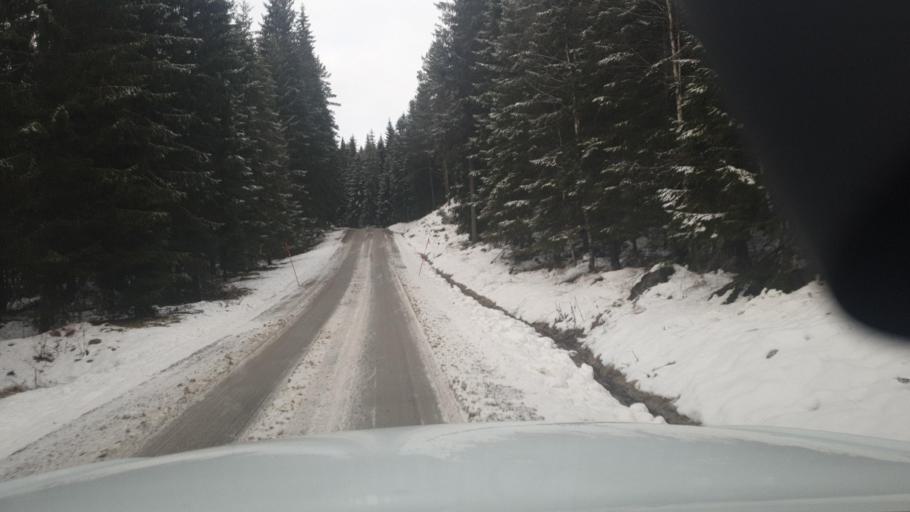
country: SE
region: Vaermland
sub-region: Sunne Kommun
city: Sunne
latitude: 59.8573
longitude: 12.8443
